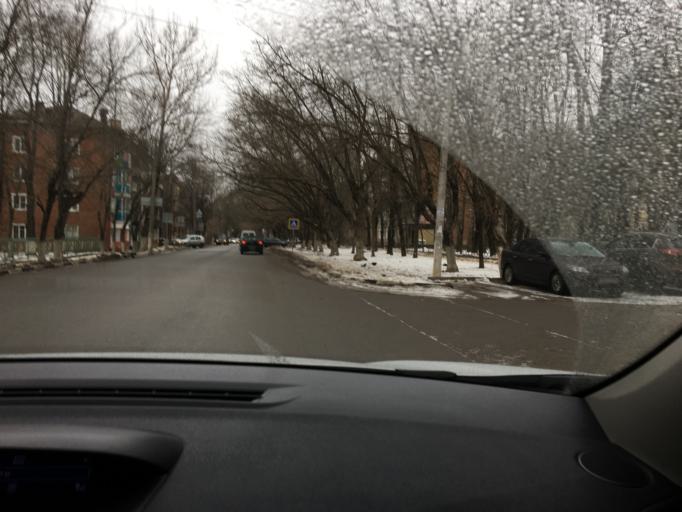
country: RU
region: Tula
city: Mendeleyevskiy
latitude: 54.1638
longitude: 37.5770
